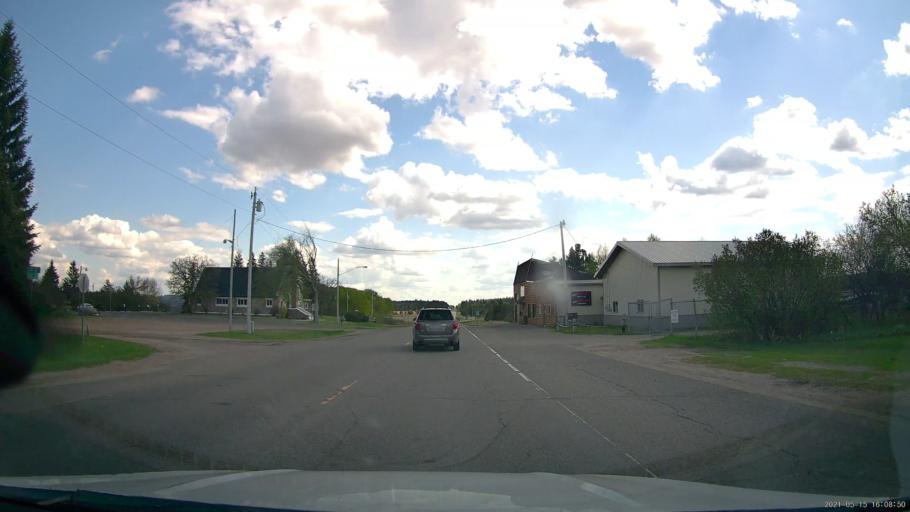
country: US
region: Minnesota
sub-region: Hubbard County
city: Park Rapids
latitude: 46.9560
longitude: -94.9527
